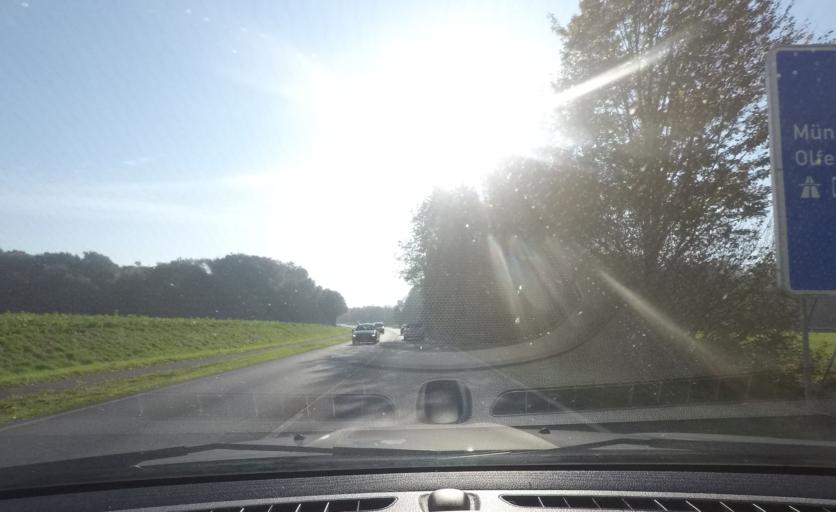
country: DE
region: North Rhine-Westphalia
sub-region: Regierungsbezirk Munster
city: Dulmen
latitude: 51.8471
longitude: 7.2531
